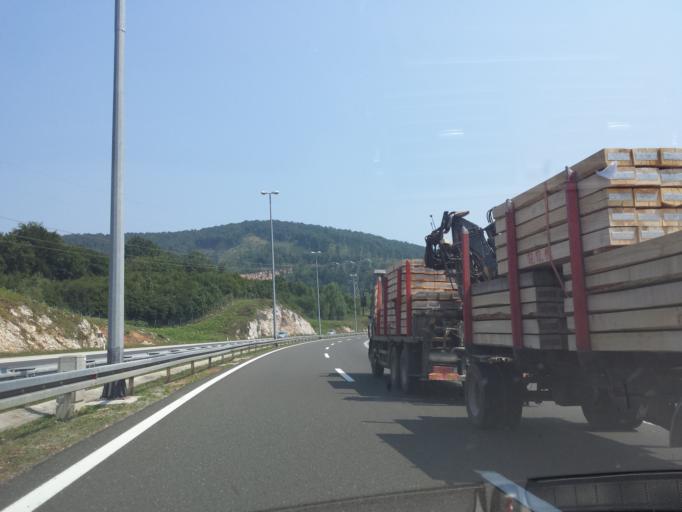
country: HR
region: Karlovacka
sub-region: Grad Ogulin
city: Ogulin
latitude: 45.4067
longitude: 15.2510
